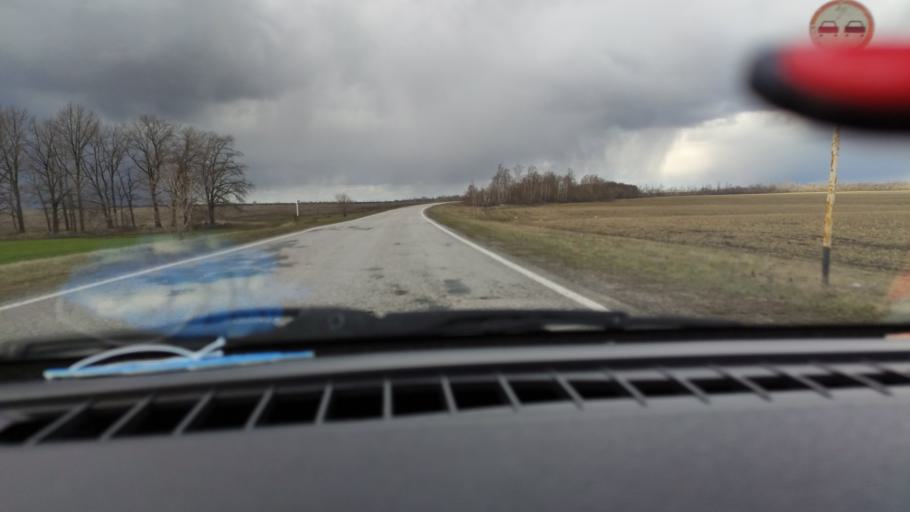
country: RU
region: Samara
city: Povolzhskiy
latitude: 53.7936
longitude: 49.7512
